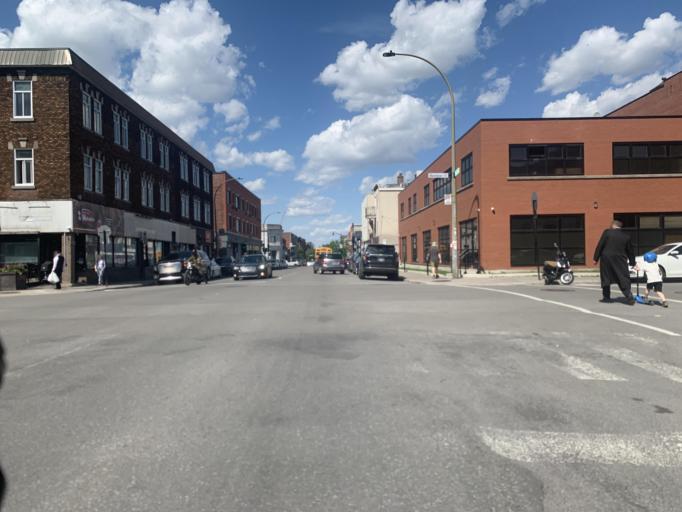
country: CA
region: Quebec
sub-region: Montreal
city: Montreal
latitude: 45.5228
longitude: -73.6063
